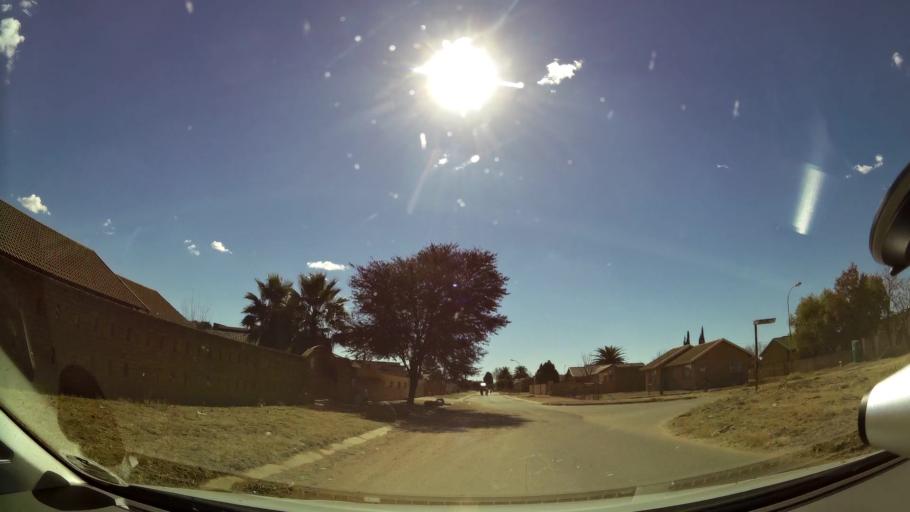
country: ZA
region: North-West
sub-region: Dr Kenneth Kaunda District Municipality
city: Klerksdorp
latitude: -26.8747
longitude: 26.5832
